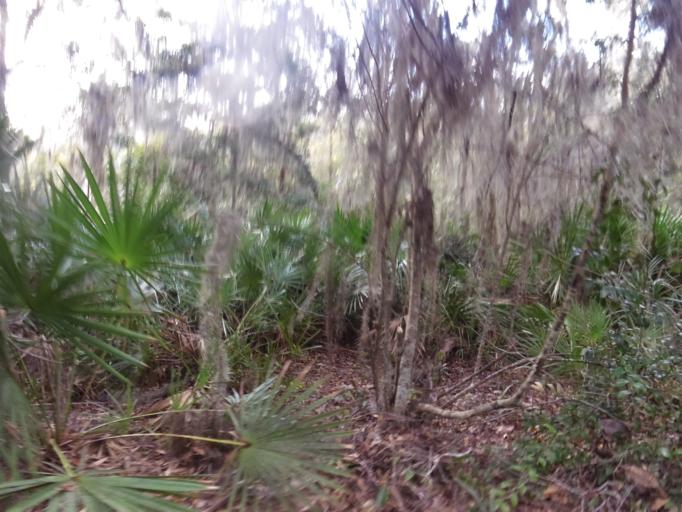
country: US
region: Florida
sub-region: Duval County
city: Atlantic Beach
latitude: 30.3816
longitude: -81.5010
